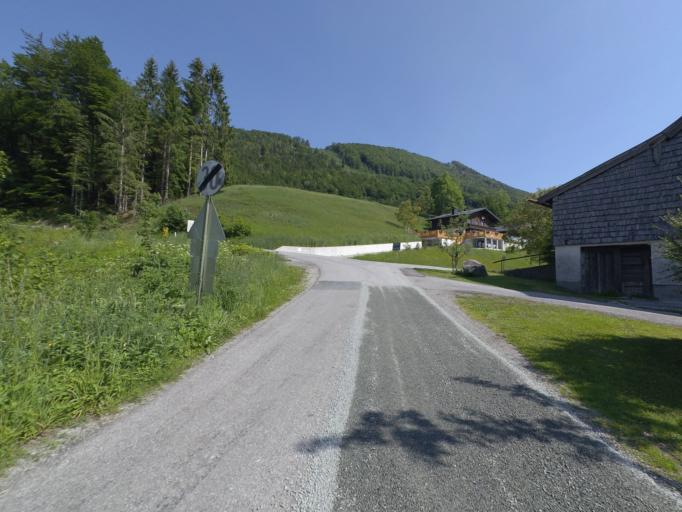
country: AT
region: Salzburg
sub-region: Politischer Bezirk Salzburg-Umgebung
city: Koppl
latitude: 47.7757
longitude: 13.1369
